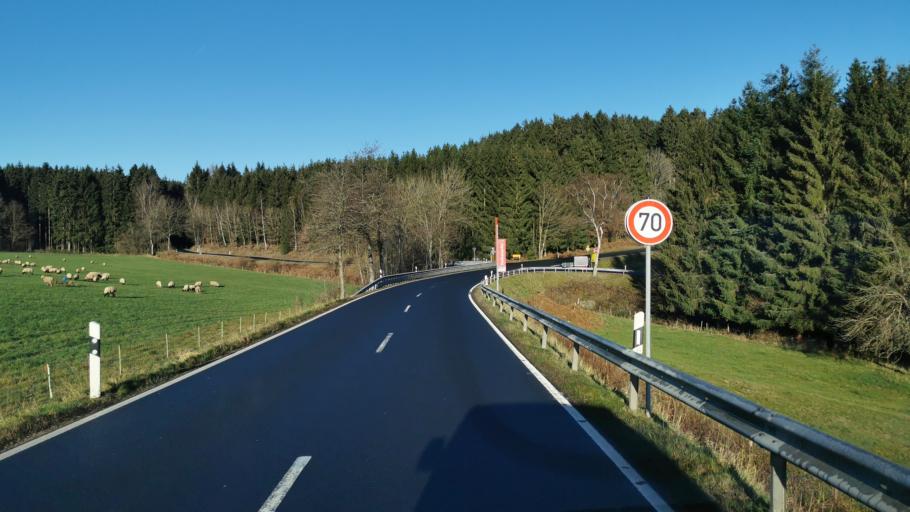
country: DE
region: Rheinland-Pfalz
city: Meisburg
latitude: 50.1118
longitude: 6.6831
